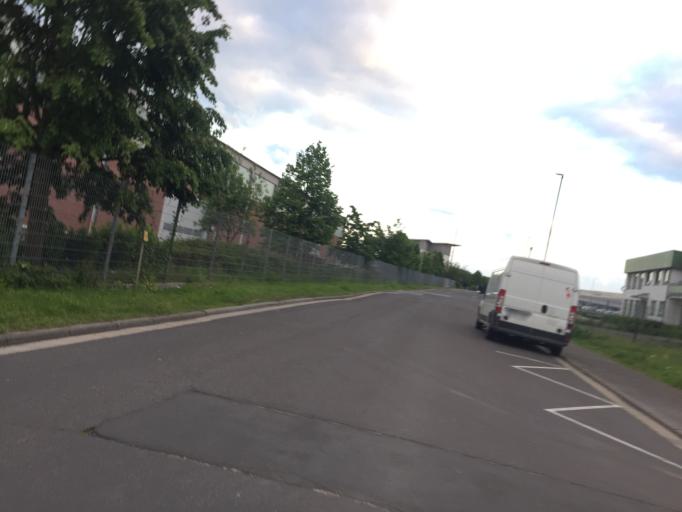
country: DE
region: Hesse
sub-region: Regierungsbezirk Darmstadt
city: Butzbach
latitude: 50.4337
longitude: 8.6885
